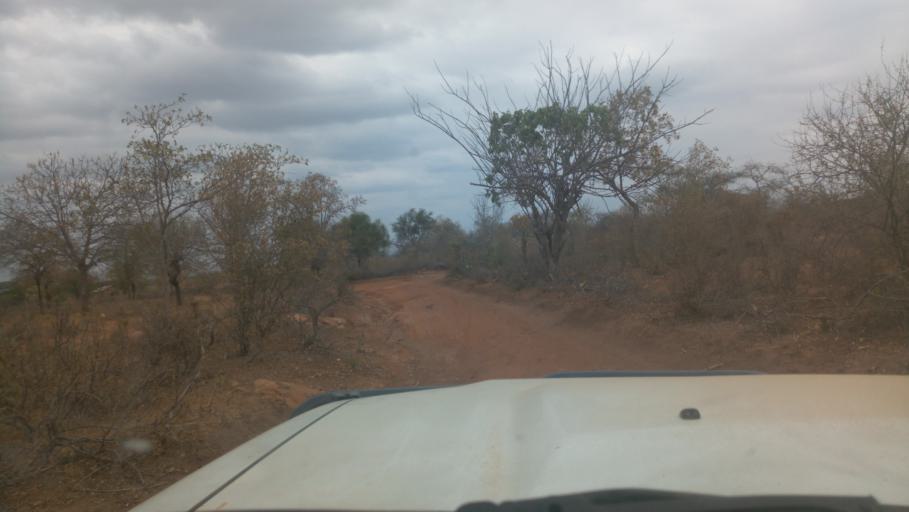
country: KE
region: Kitui
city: Kitui
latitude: -1.5795
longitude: 37.9226
